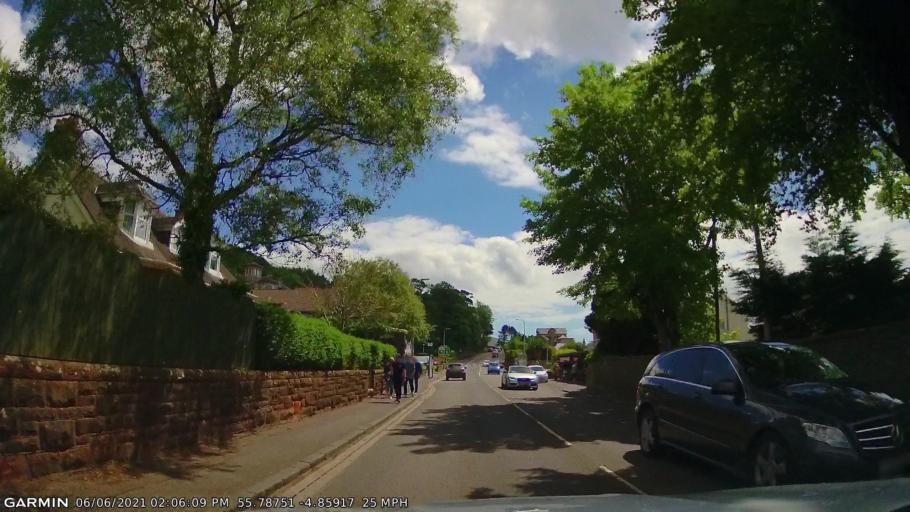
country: GB
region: Scotland
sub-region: North Ayrshire
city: Largs
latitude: 55.7875
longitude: -4.8592
